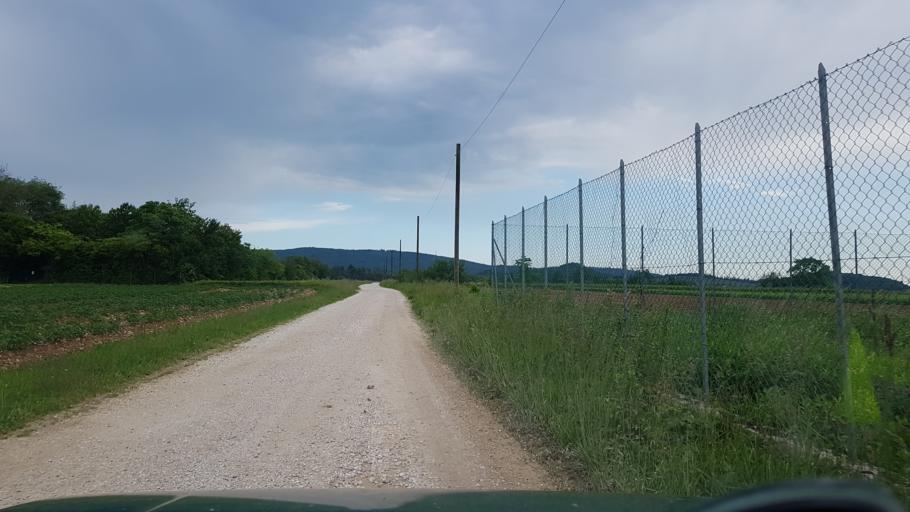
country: IT
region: Friuli Venezia Giulia
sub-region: Provincia di Gorizia
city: Mossa
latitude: 45.9291
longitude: 13.5426
